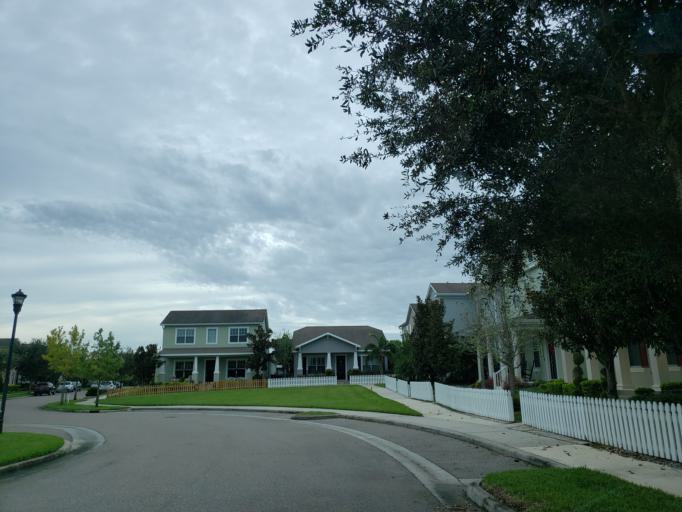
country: US
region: Florida
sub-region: Hillsborough County
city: Riverview
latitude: 27.8905
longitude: -82.3145
